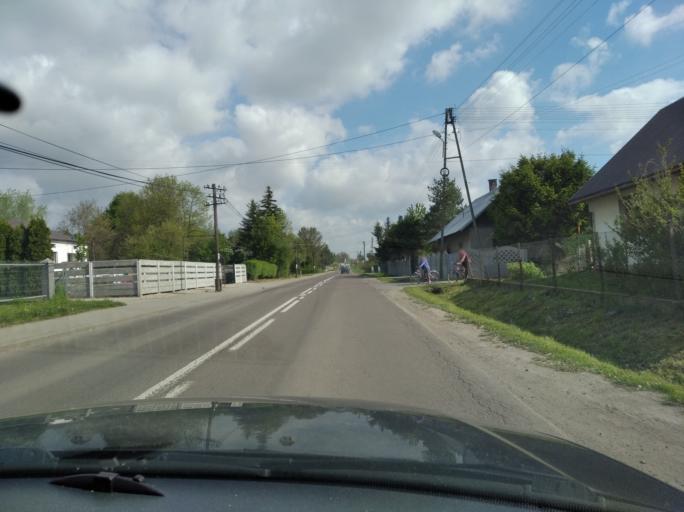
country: PL
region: Subcarpathian Voivodeship
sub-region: Powiat przeworski
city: Urzejowice
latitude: 50.0161
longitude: 22.4619
